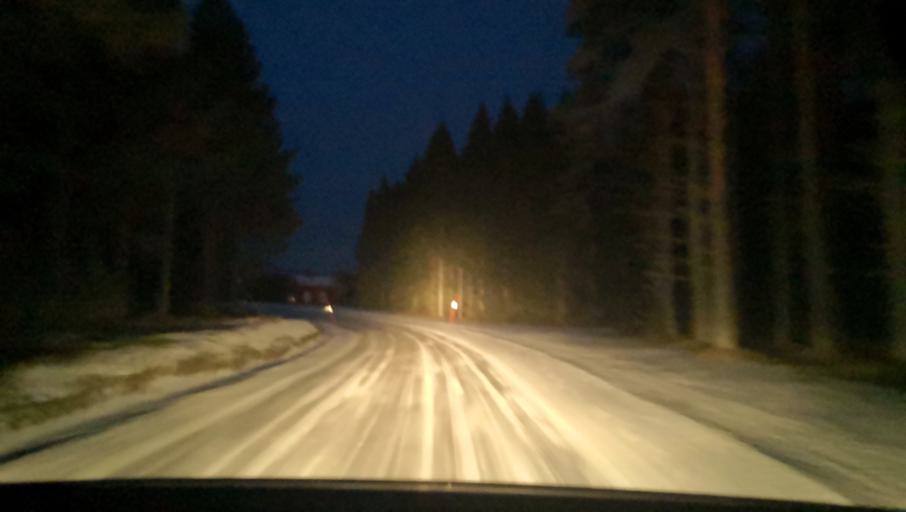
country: SE
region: Uppsala
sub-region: Heby Kommun
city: Tarnsjo
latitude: 60.2715
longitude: 16.7973
